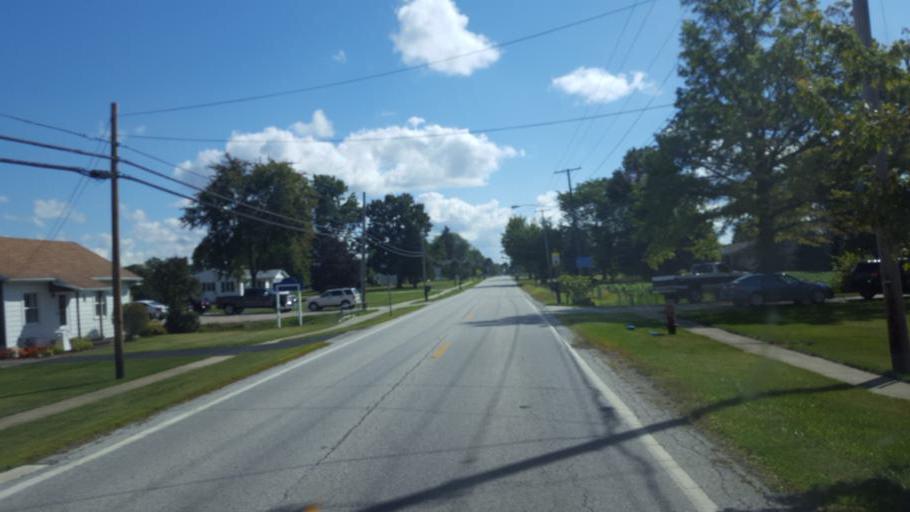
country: US
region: Ohio
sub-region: Lorain County
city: Lagrange
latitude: 41.2373
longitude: -82.1107
